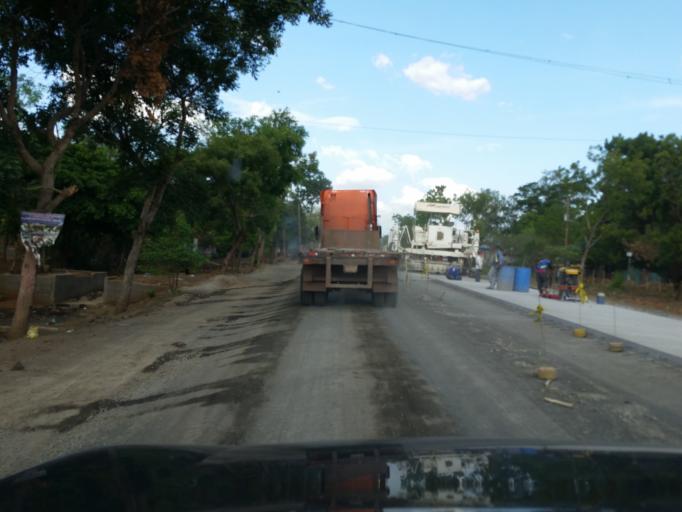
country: NI
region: Managua
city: Carlos Fonseca Amador
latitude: 12.0676
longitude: -86.4801
